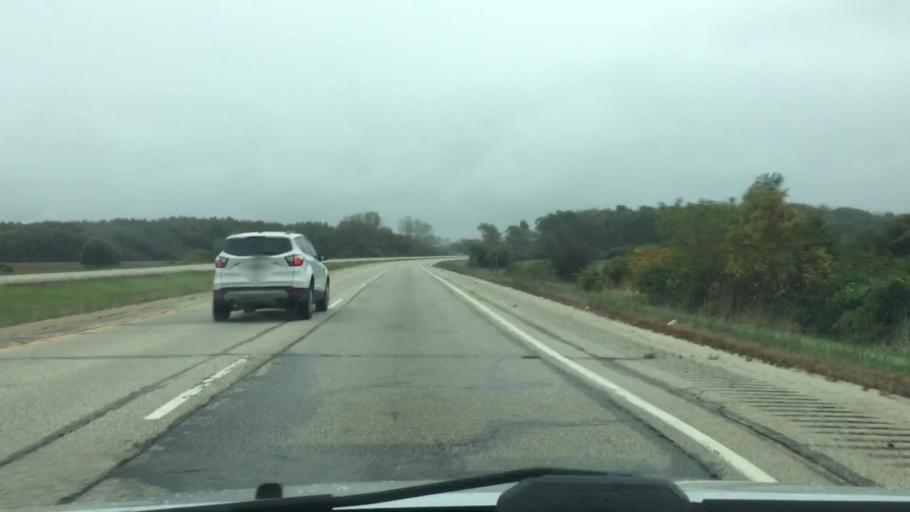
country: US
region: Wisconsin
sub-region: Walworth County
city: Como
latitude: 42.6357
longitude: -88.4802
